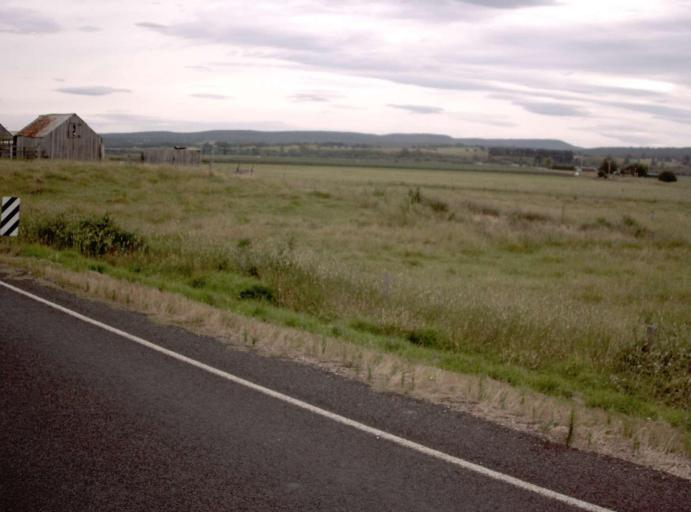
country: AU
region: Victoria
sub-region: East Gippsland
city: Bairnsdale
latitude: -37.8163
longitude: 147.4922
